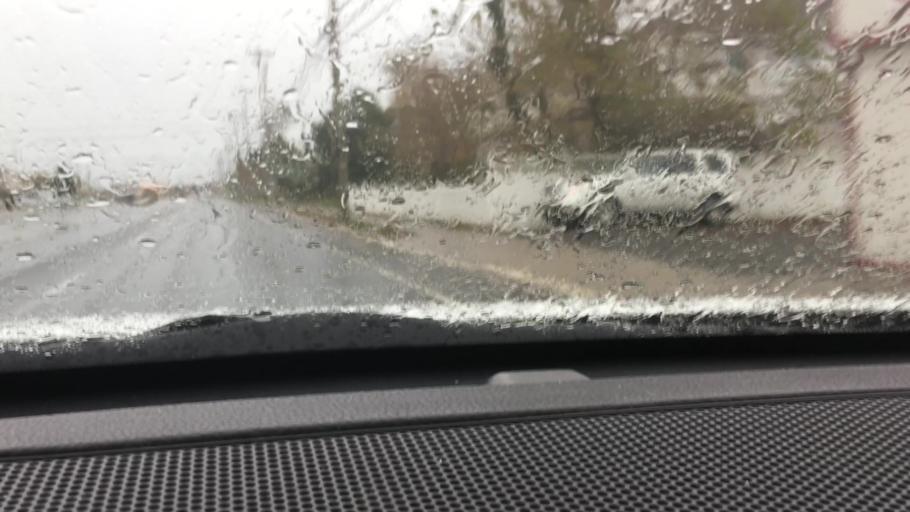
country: US
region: New Jersey
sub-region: Atlantic County
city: Pleasantville
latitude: 39.3877
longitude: -74.5182
